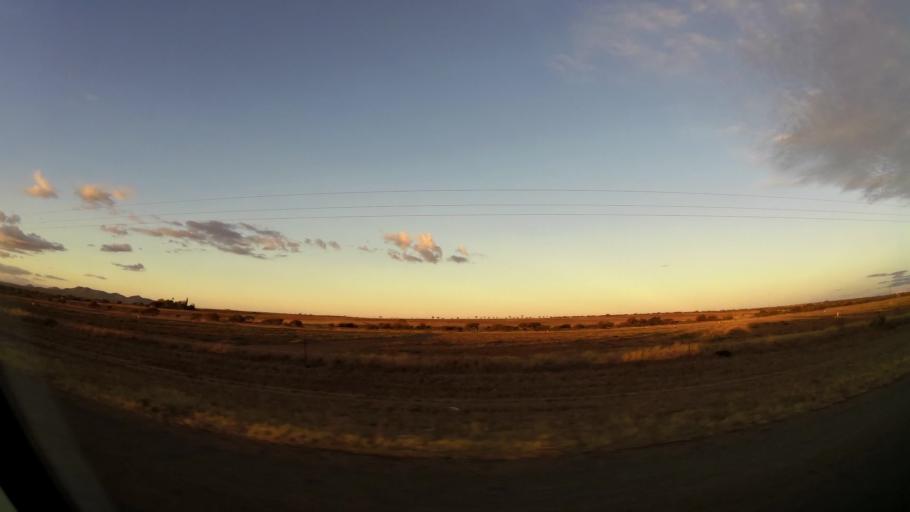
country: ZA
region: Limpopo
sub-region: Capricorn District Municipality
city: Polokwane
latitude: -23.7859
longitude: 29.4756
